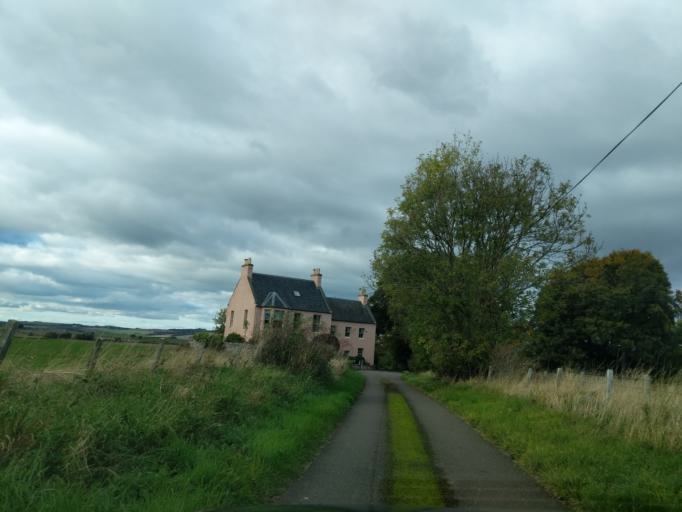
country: GB
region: Scotland
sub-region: East Lothian
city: East Linton
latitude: 55.9412
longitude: -2.7113
